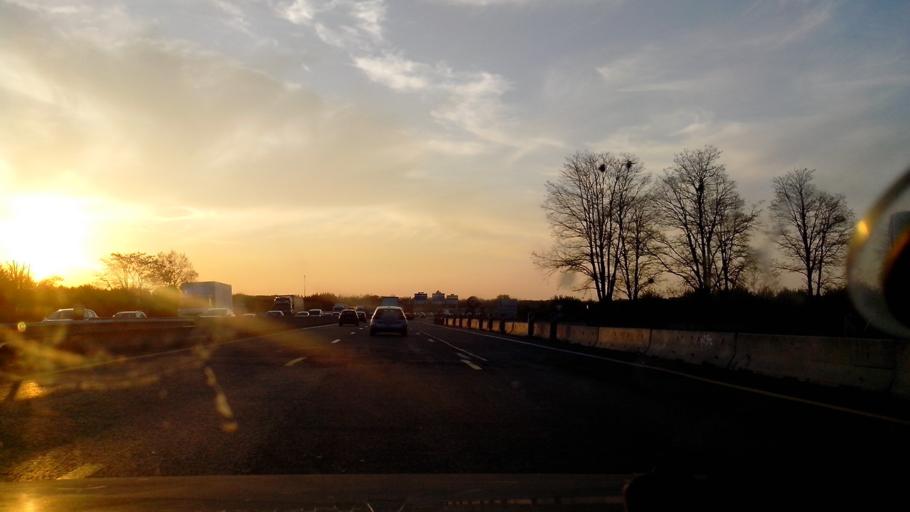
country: FR
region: Ile-de-France
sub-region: Departement de Seine-et-Marne
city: Emerainville
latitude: 48.8162
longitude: 2.6227
